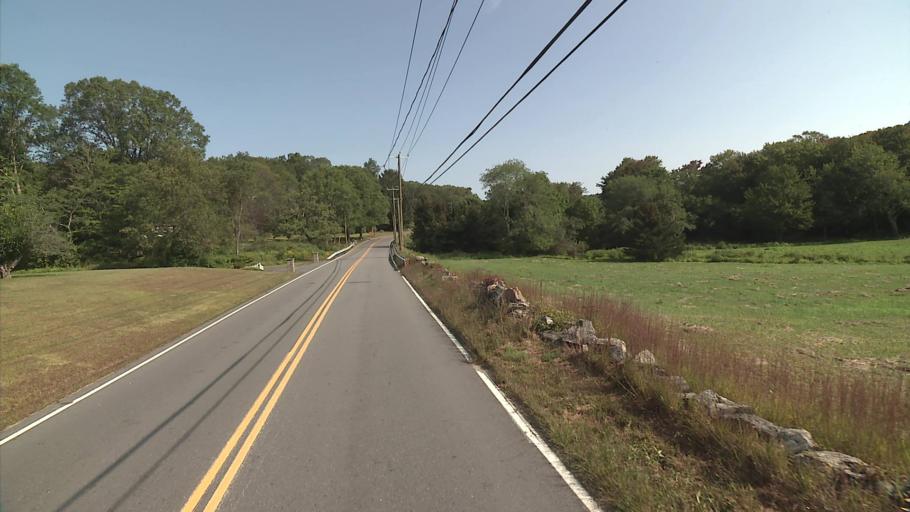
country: US
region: Connecticut
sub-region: New London County
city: Lisbon
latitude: 41.5763
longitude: -72.0300
